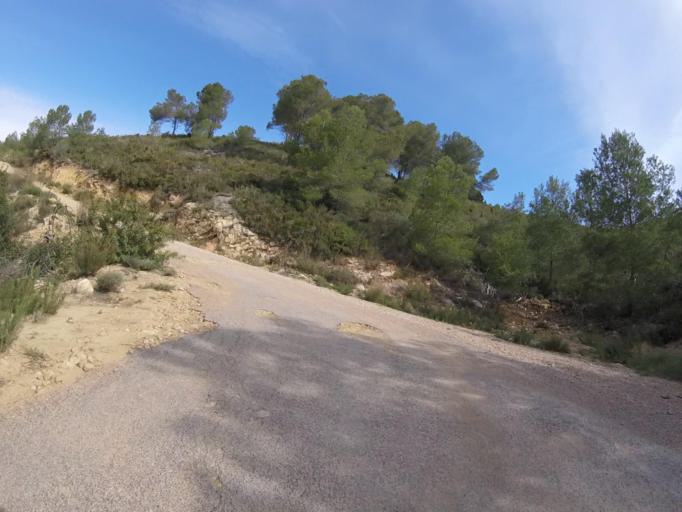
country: ES
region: Valencia
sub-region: Provincia de Castello
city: Torreblanca
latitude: 40.2039
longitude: 0.1515
